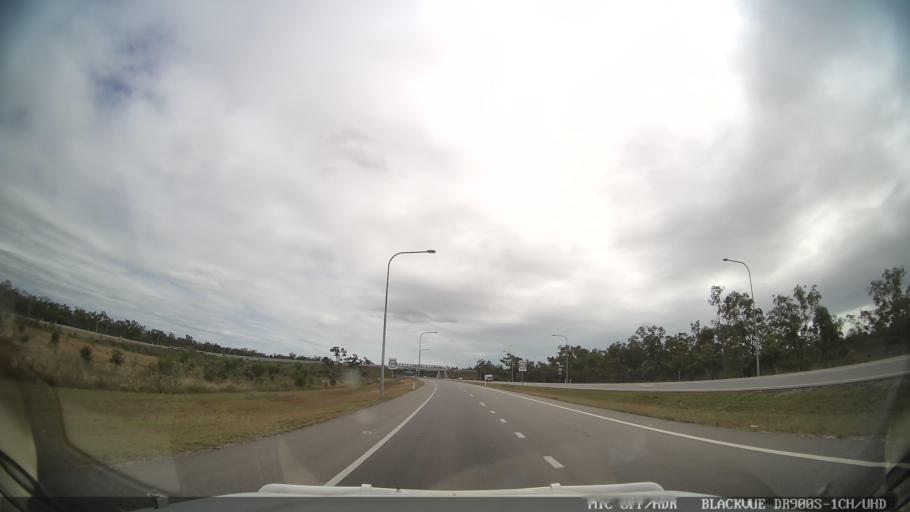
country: AU
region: Queensland
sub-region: Townsville
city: Bohle Plains
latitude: -19.2982
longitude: 146.6947
